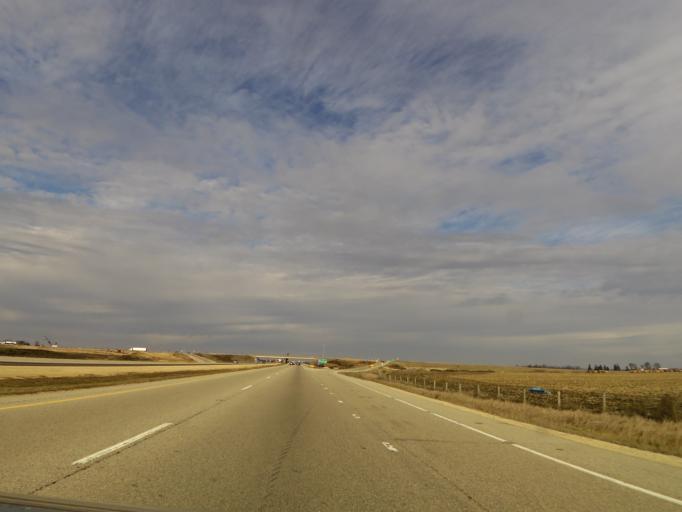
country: US
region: Wisconsin
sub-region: Rock County
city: Janesville
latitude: 42.6299
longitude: -88.9826
